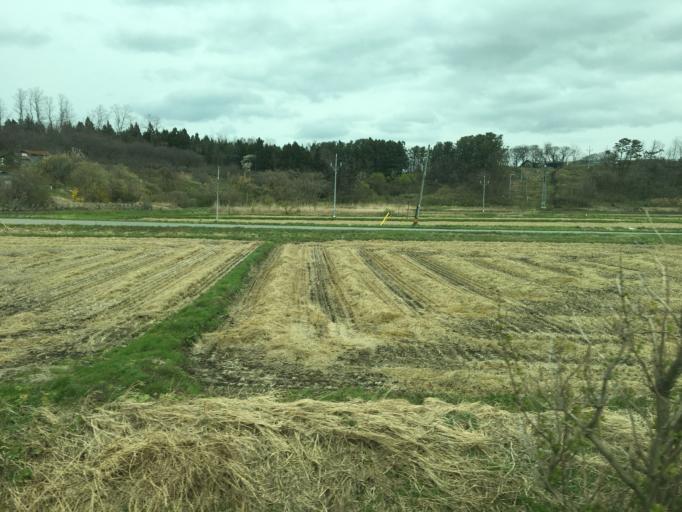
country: JP
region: Aomori
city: Shimokizukuri
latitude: 40.7840
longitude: 140.2556
